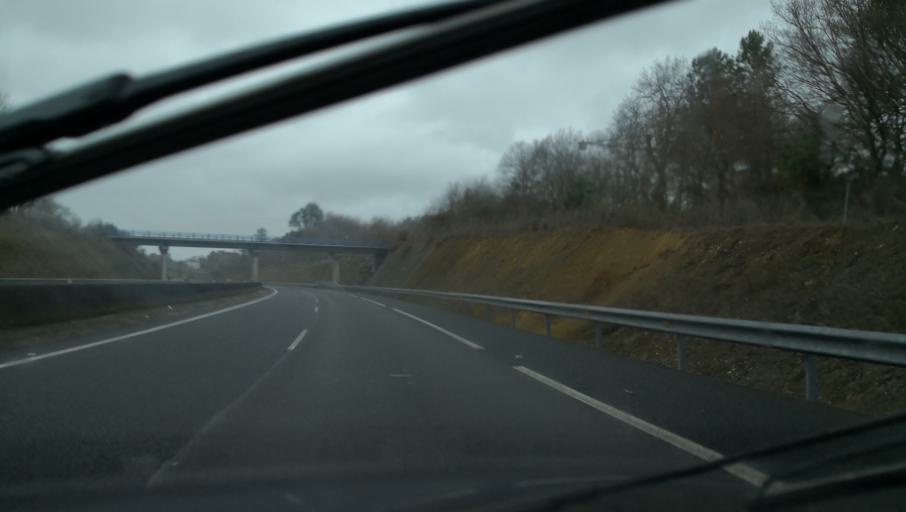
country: ES
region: Galicia
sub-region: Provincia de Pontevedra
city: Lalin
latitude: 42.6819
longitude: -8.1625
